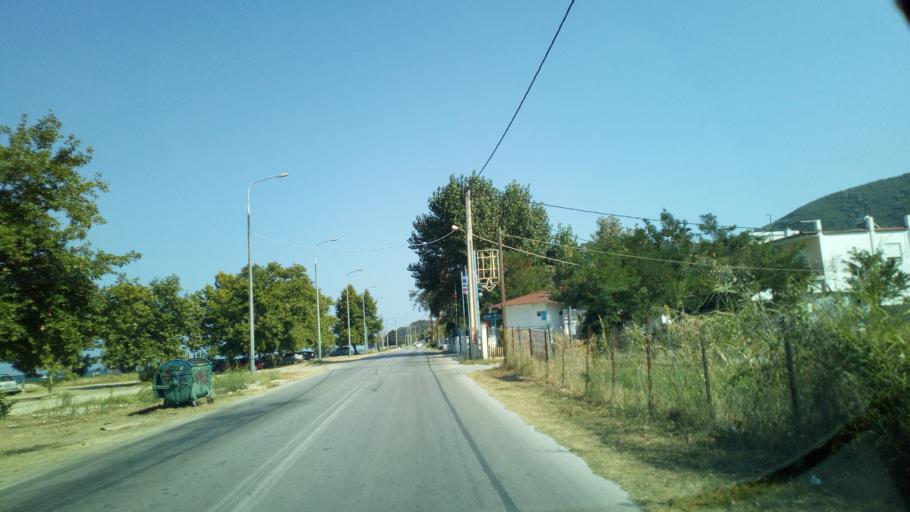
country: GR
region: Central Macedonia
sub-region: Nomos Thessalonikis
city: Stavros
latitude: 40.6619
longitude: 23.7195
